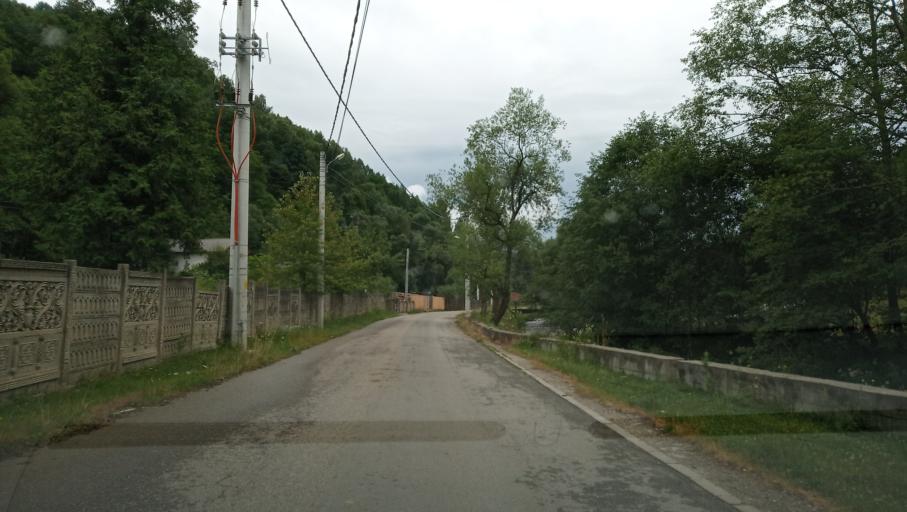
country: RO
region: Hunedoara
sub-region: Oras Petrila
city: Petrila
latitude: 45.4661
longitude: 23.4196
